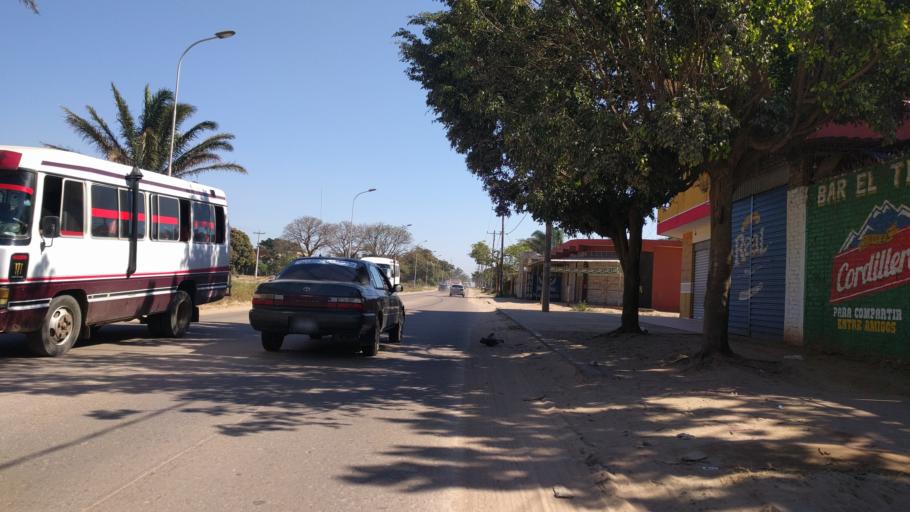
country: BO
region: Santa Cruz
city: Santa Cruz de la Sierra
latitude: -17.8451
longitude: -63.2106
